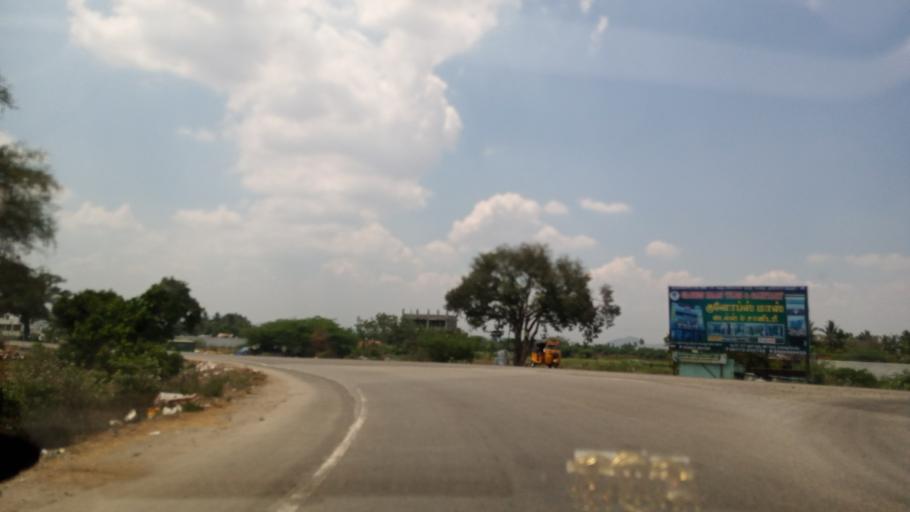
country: IN
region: Tamil Nadu
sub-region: Vellore
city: Walajapet
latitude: 12.9178
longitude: 79.3861
